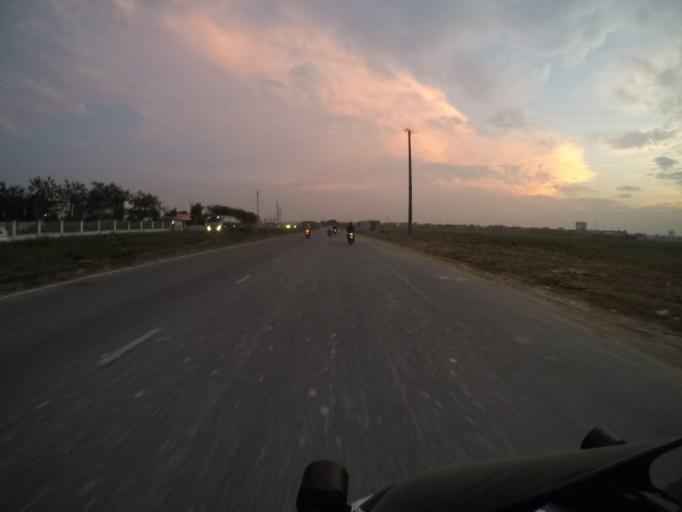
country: VN
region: Vinh Phuc
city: Phuc Yen
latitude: 21.2476
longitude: 105.7216
